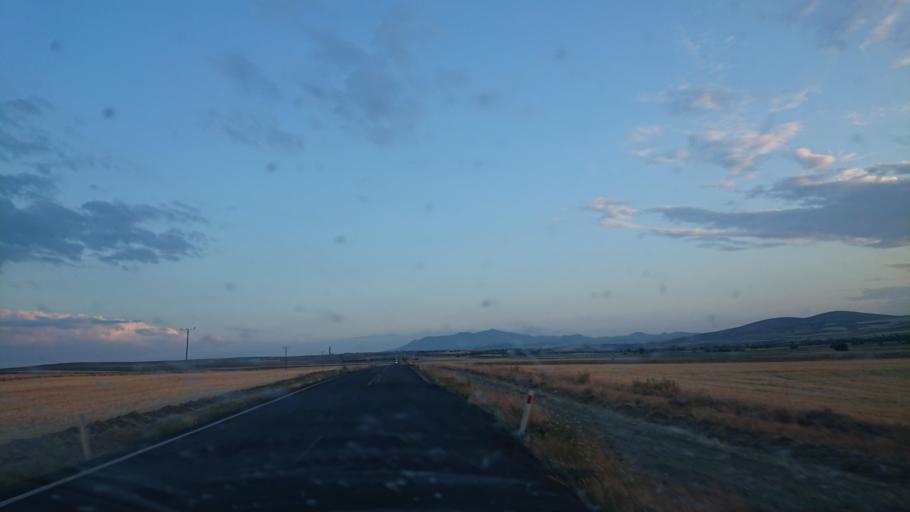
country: TR
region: Aksaray
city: Balci
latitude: 38.8197
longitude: 34.1352
